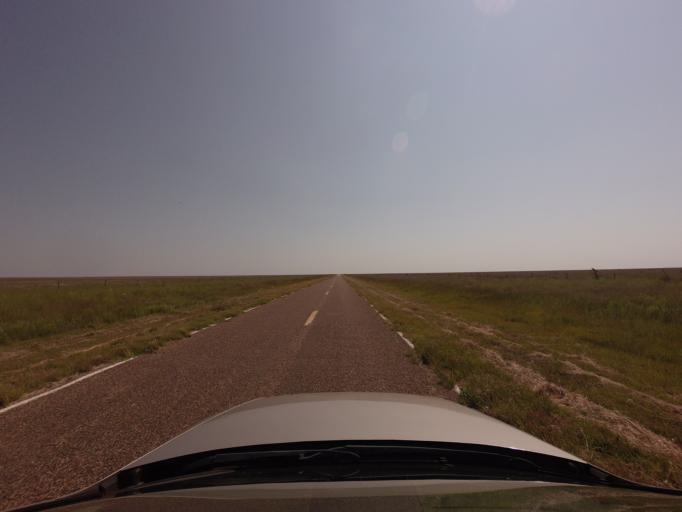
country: US
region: New Mexico
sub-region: Curry County
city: Cannon Air Force Base
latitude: 34.6333
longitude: -103.4533
